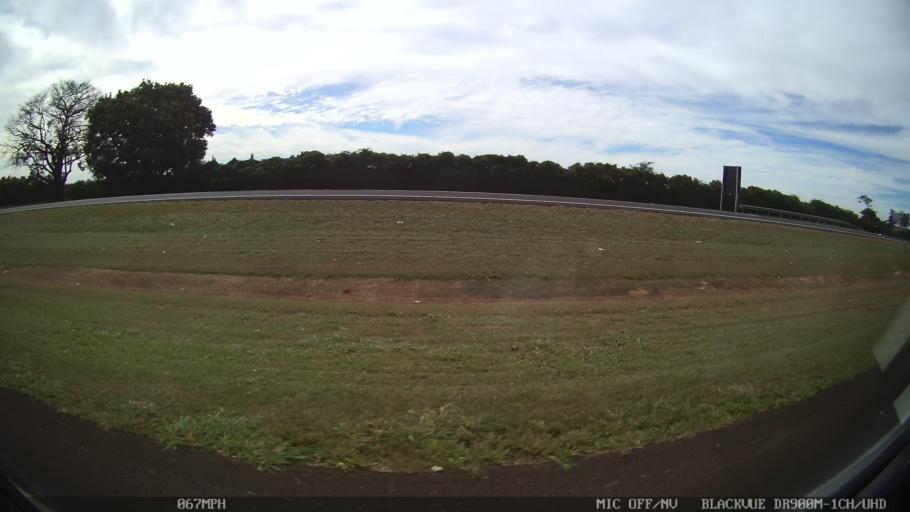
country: BR
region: Sao Paulo
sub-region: Taquaritinga
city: Taquaritinga
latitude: -21.4631
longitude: -48.6167
